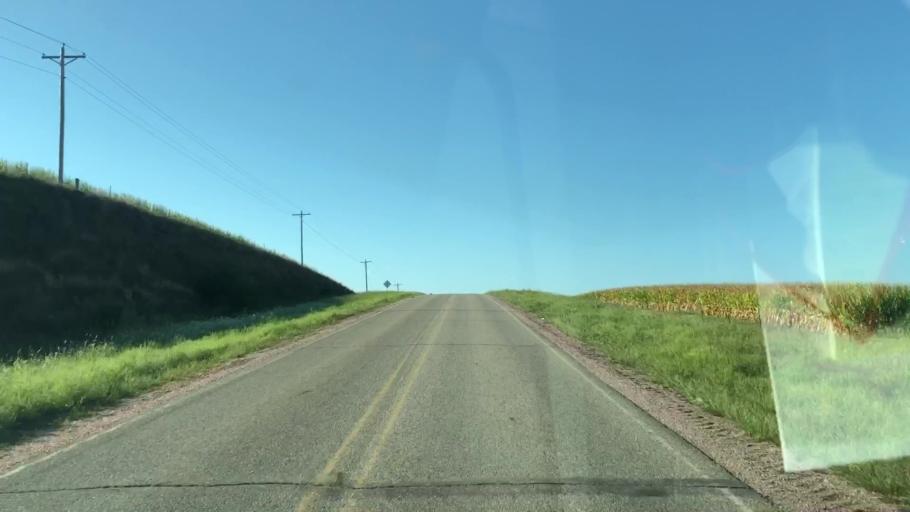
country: US
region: Iowa
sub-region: Woodbury County
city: Moville
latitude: 42.4738
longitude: -96.2136
